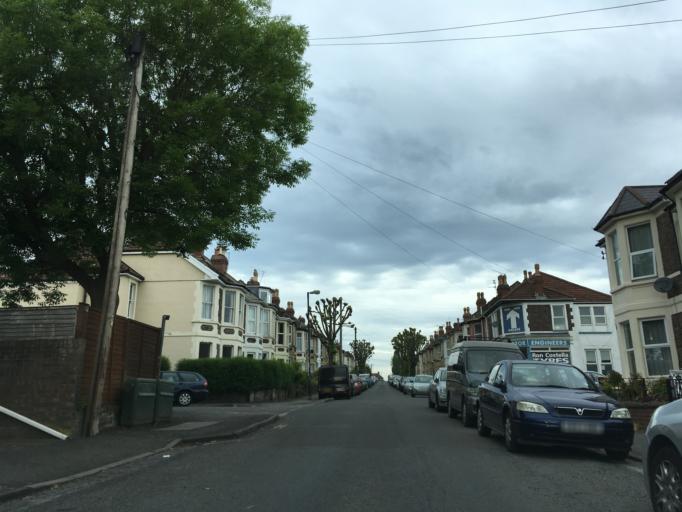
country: GB
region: England
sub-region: Bristol
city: Bristol
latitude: 51.4797
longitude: -2.5962
